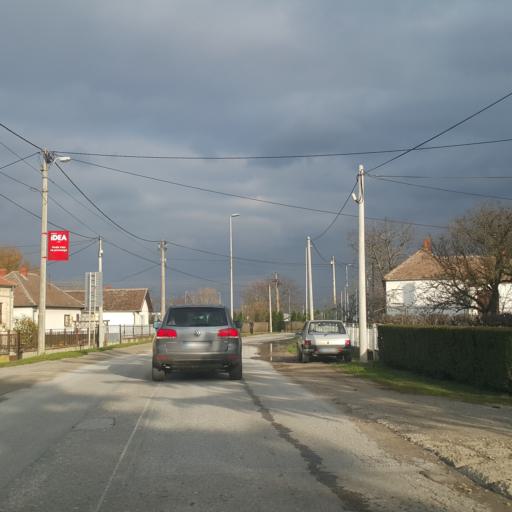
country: RS
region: Central Serbia
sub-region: Sumadijski Okrug
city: Lapovo
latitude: 44.2384
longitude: 21.1142
